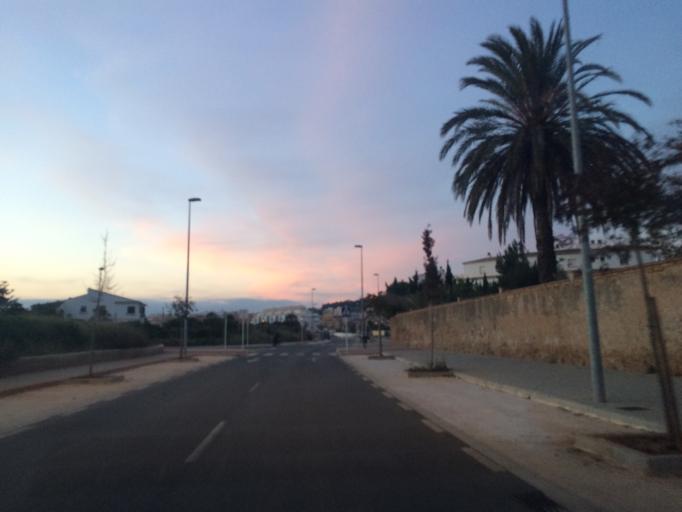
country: ES
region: Valencia
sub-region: Provincia de Alicante
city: Denia
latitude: 38.8337
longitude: 0.1166
